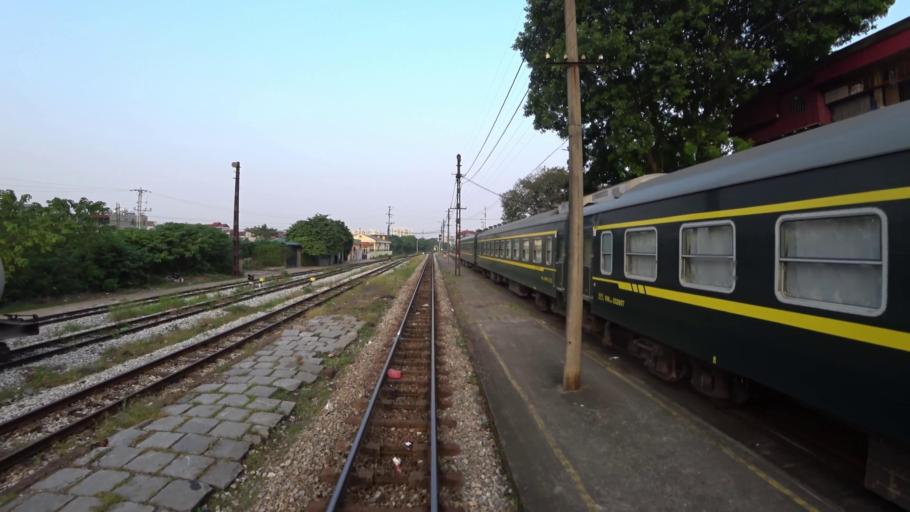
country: VN
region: Ha Noi
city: Hoan Kiem
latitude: 21.0658
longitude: 105.8971
